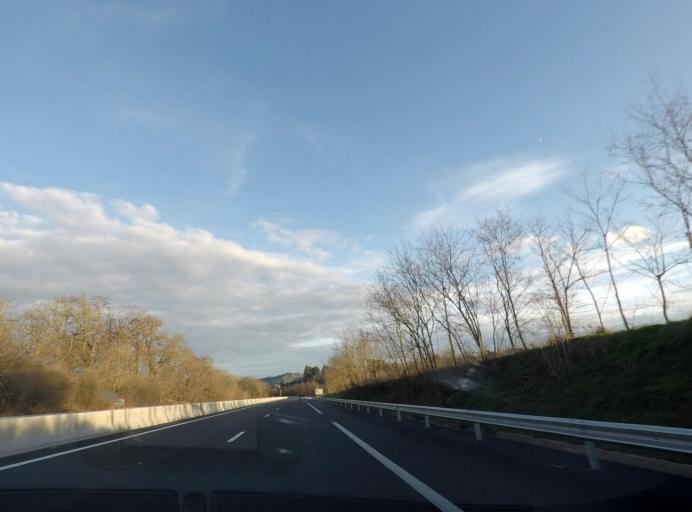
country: FR
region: Bourgogne
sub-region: Departement de Saone-et-Loire
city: Matour
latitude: 46.3830
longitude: 4.4726
